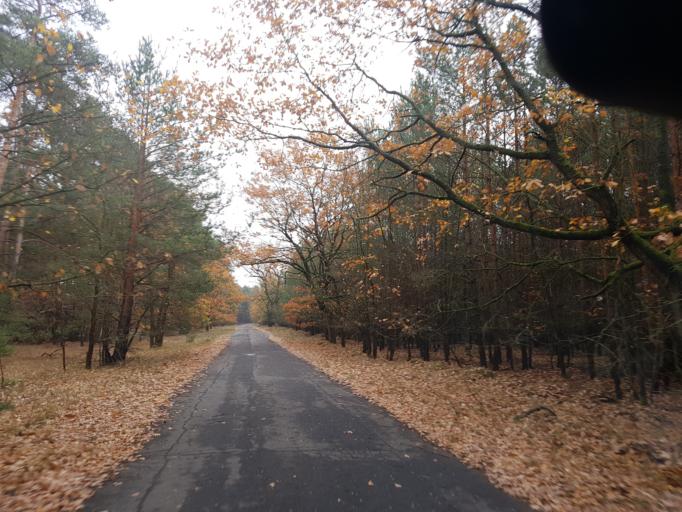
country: DE
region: Brandenburg
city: Treuenbrietzen
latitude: 52.1073
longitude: 12.9104
